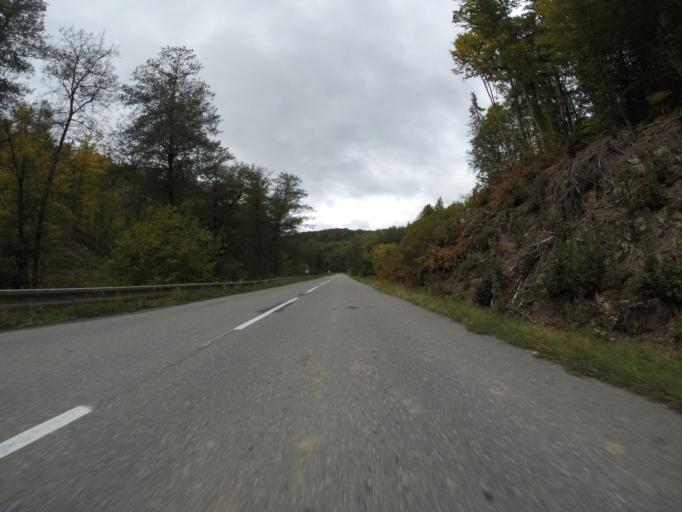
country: SK
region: Banskobystricky
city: Poltar
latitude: 48.5904
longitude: 19.7873
